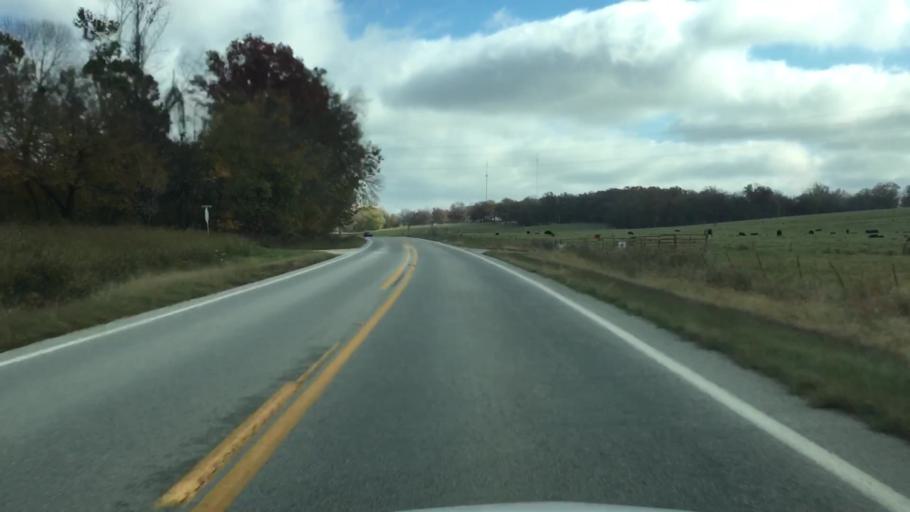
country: US
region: Arkansas
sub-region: Benton County
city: Gentry
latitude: 36.2578
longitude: -94.4046
